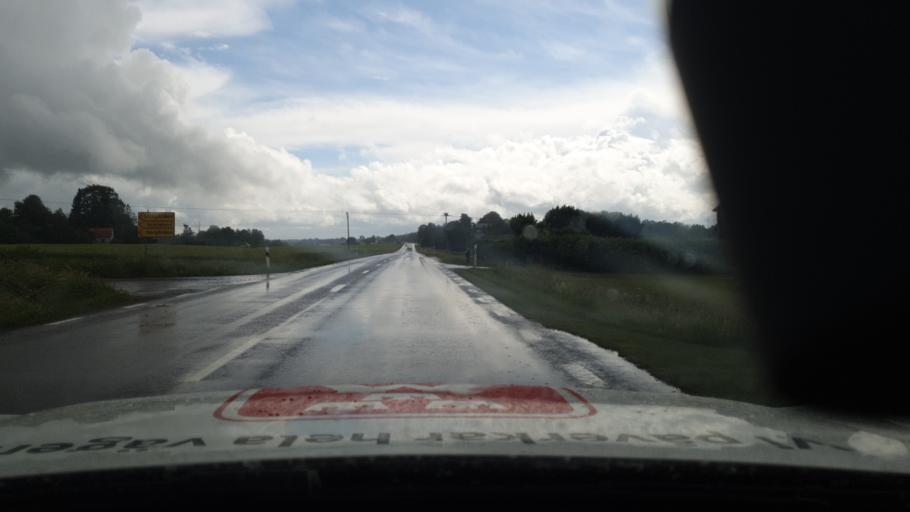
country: SE
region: Vaestra Goetaland
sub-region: Falkopings Kommun
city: Falkoeping
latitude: 58.1061
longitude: 13.5360
